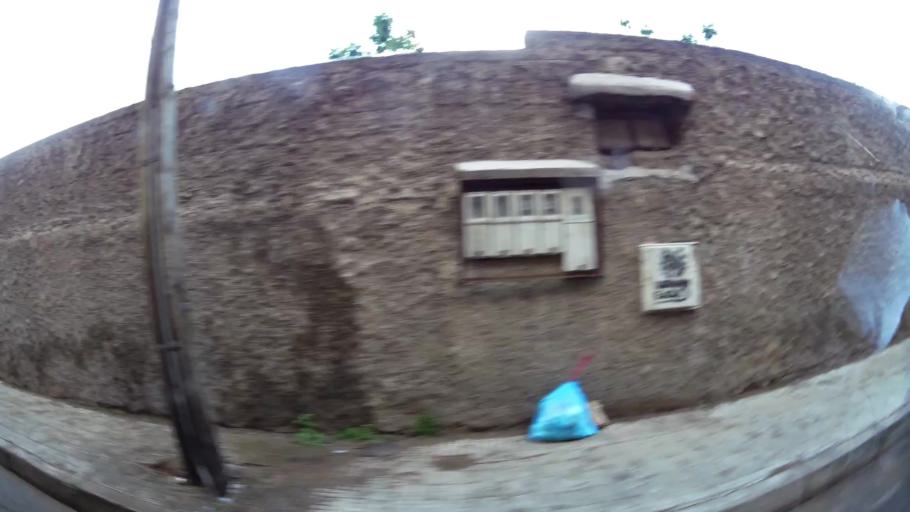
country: MA
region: Grand Casablanca
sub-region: Casablanca
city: Casablanca
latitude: 33.5471
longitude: -7.5883
